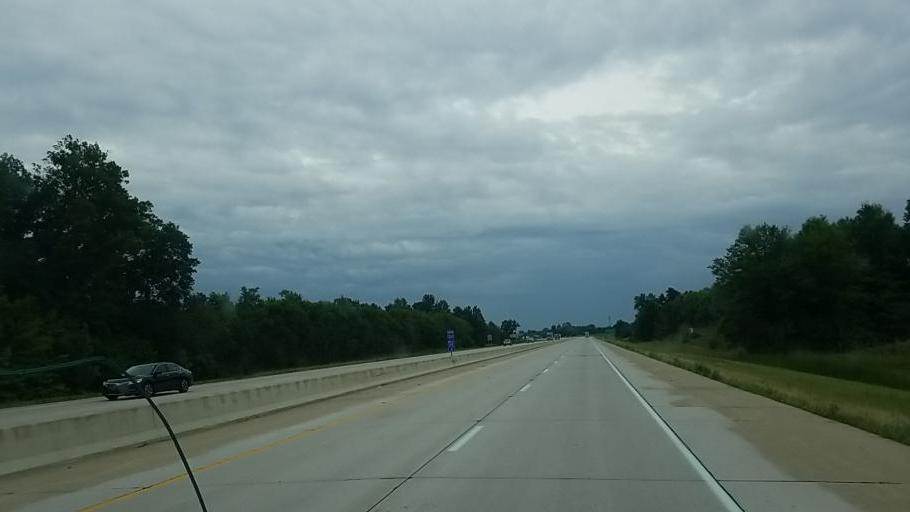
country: US
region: Indiana
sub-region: Allen County
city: Leo-Cedarville
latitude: 41.1464
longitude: -85.0150
